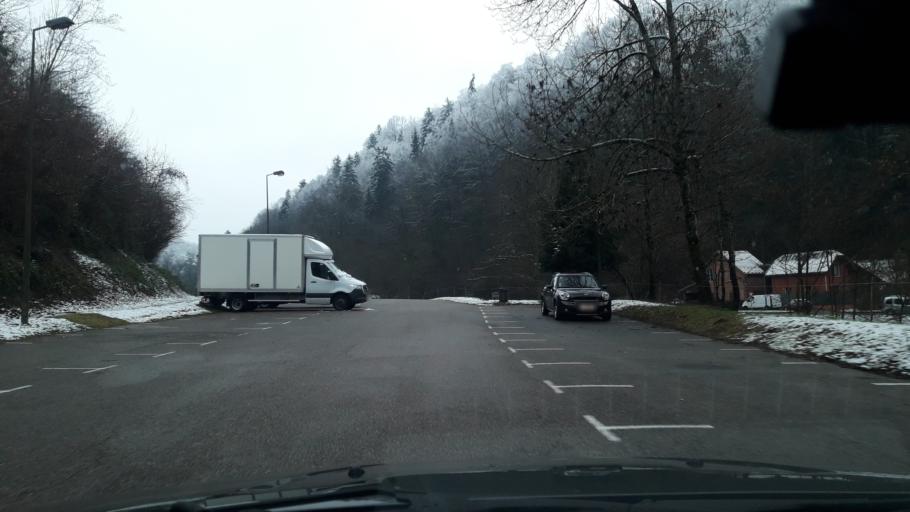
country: FR
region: Rhone-Alpes
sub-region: Departement de l'Isere
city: Vaulnaveys-le-Haut
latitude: 45.1459
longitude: 5.8295
